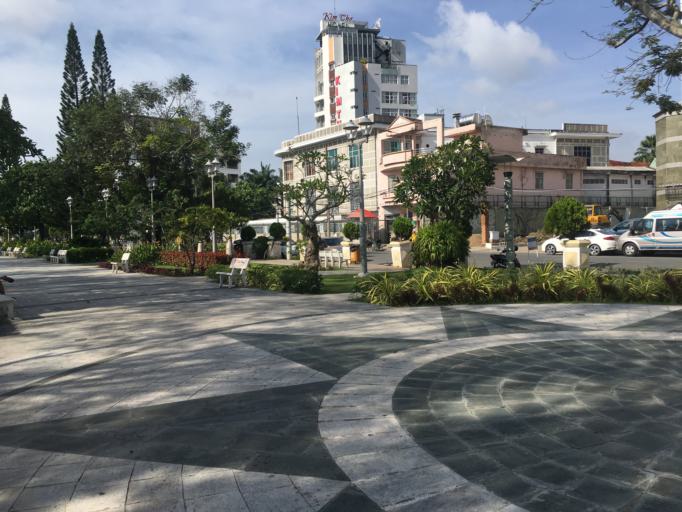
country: VN
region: Can Tho
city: Can Tho
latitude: 10.0356
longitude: 105.7897
